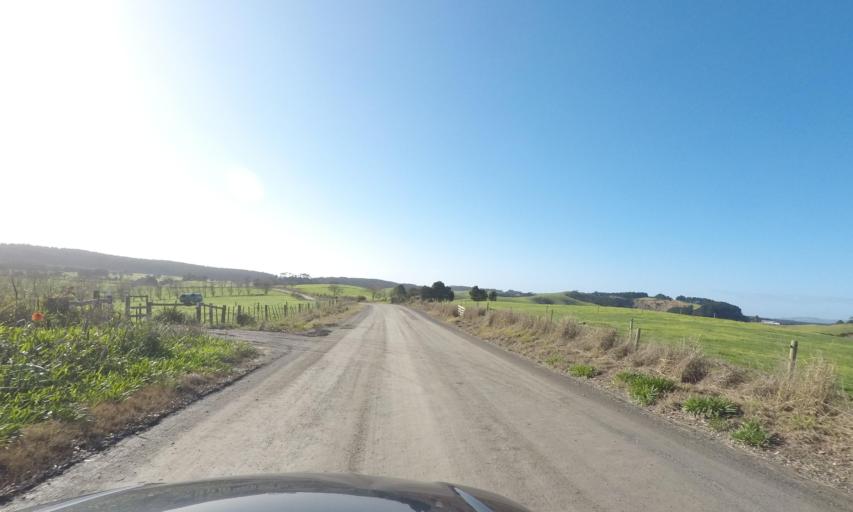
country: NZ
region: Auckland
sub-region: Auckland
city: Wellsford
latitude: -36.1614
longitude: 174.6065
